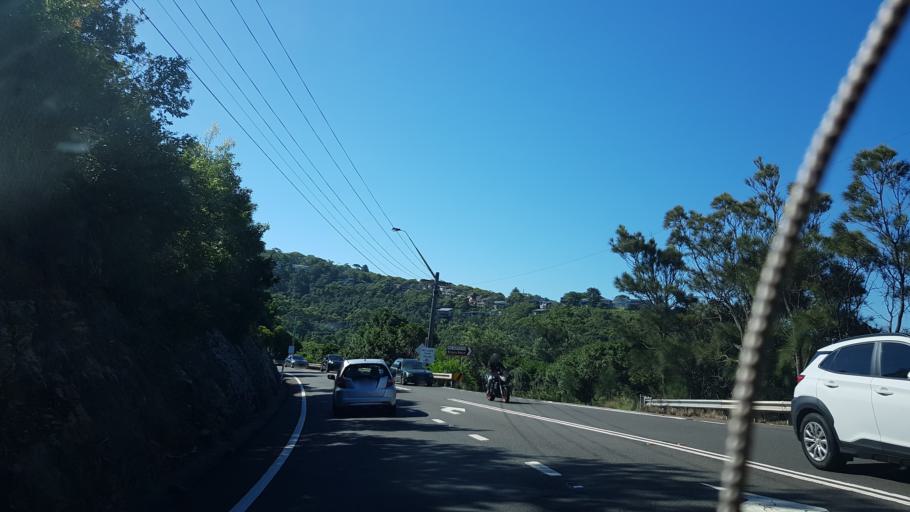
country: AU
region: New South Wales
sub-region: Pittwater
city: Bilgola Beach
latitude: -33.6479
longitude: 151.3271
